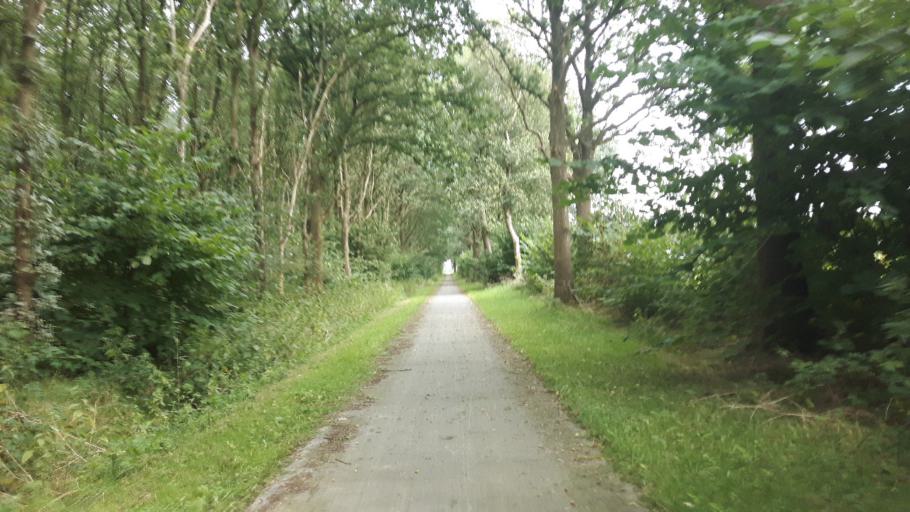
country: NL
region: Friesland
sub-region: Gemeente Weststellingwerf
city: Noordwolde
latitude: 52.9580
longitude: 6.2379
